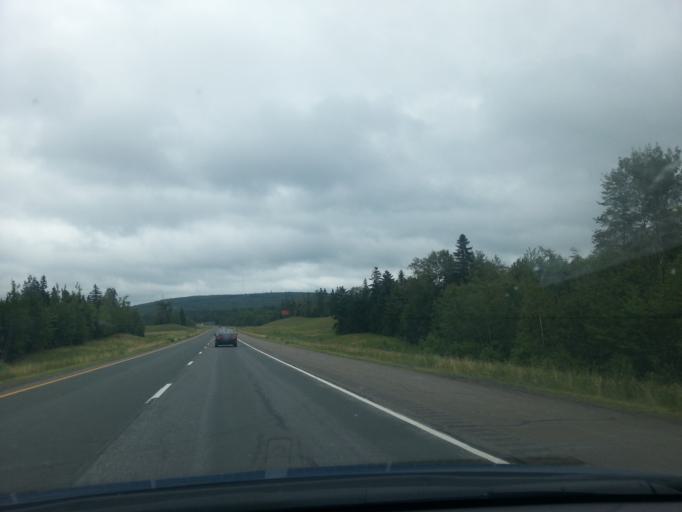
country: CA
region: New Brunswick
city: Nackawic
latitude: 45.8849
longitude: -67.0199
